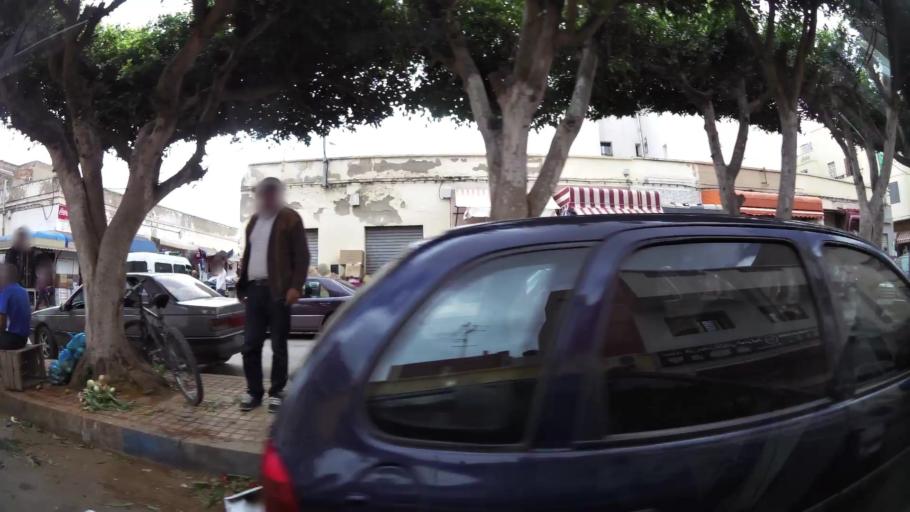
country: MA
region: Oriental
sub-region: Nador
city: Nador
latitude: 35.1781
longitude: -2.9250
